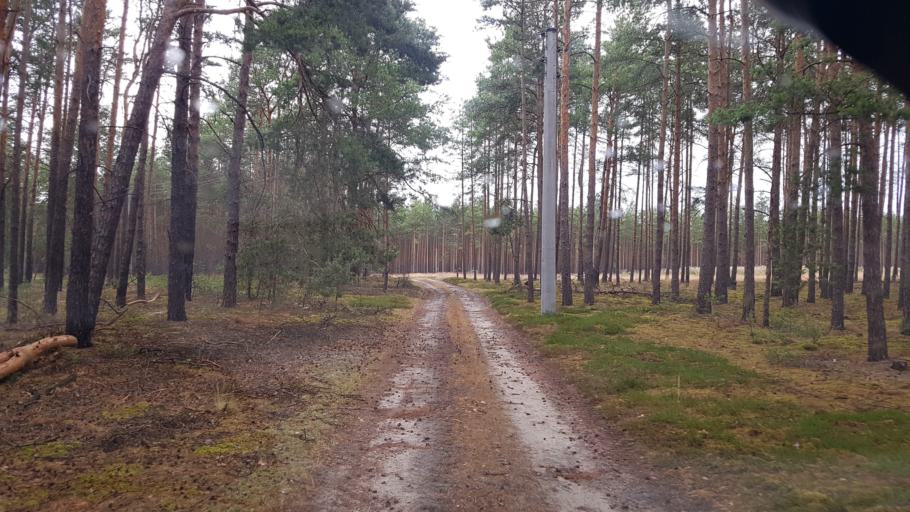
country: DE
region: Brandenburg
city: Schilda
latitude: 51.6400
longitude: 13.3521
